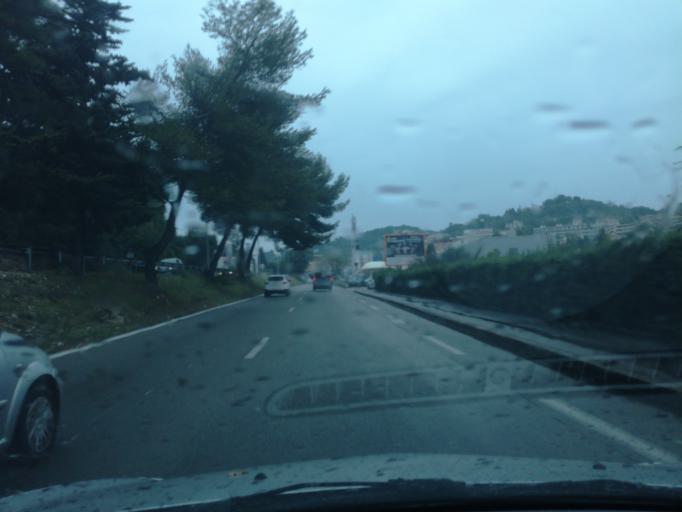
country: FR
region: Provence-Alpes-Cote d'Azur
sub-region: Departement des Alpes-Maritimes
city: Le Cannet
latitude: 43.5750
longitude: 7.0123
